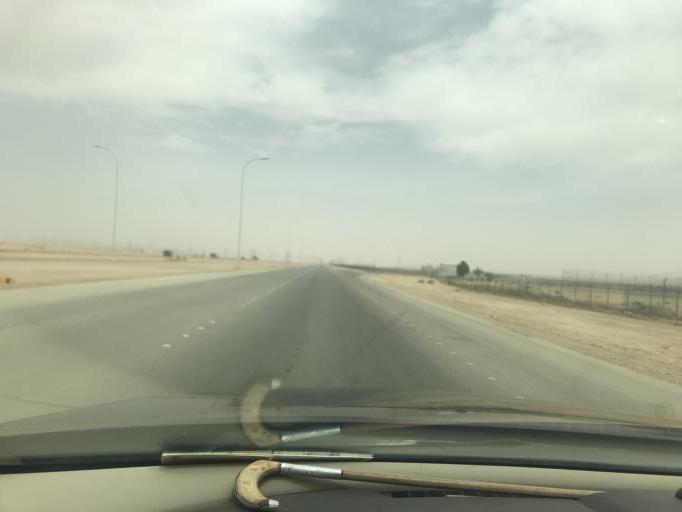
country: SA
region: Ar Riyad
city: Riyadh
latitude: 24.9618
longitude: 46.6689
